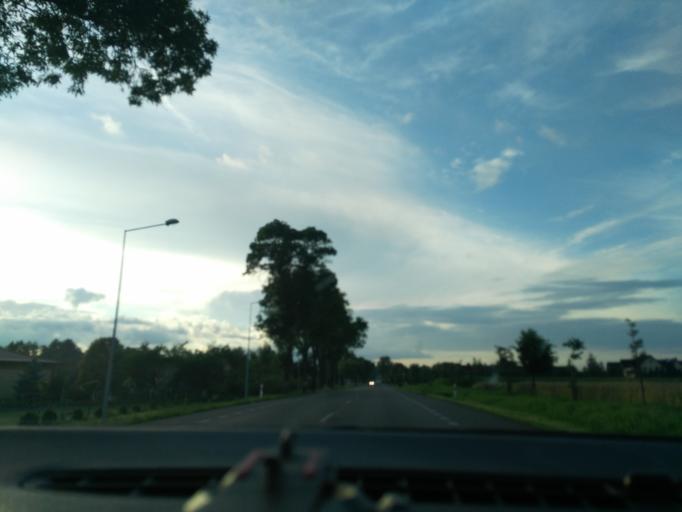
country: PL
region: Lublin Voivodeship
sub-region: Powiat lubelski
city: Niedrzwica Duza
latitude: 51.0841
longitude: 22.3703
